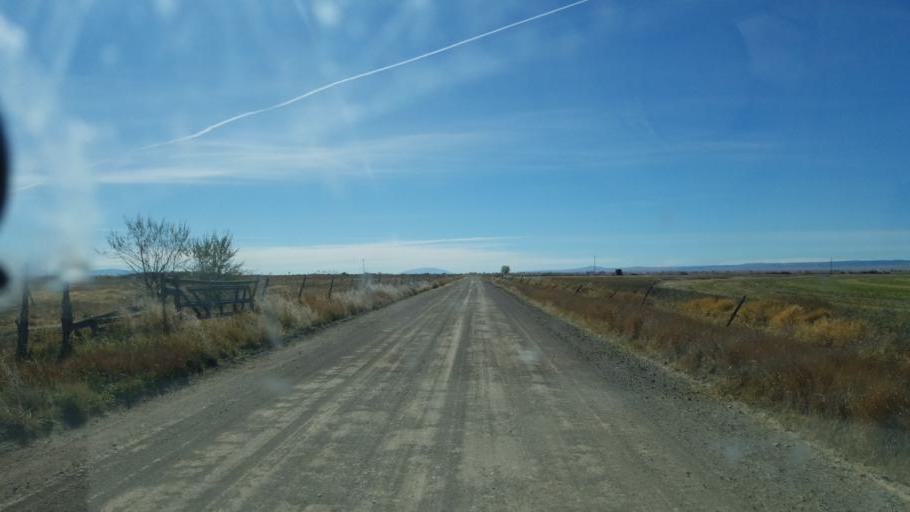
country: US
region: Colorado
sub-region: Rio Grande County
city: Monte Vista
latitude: 37.5348
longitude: -106.0758
